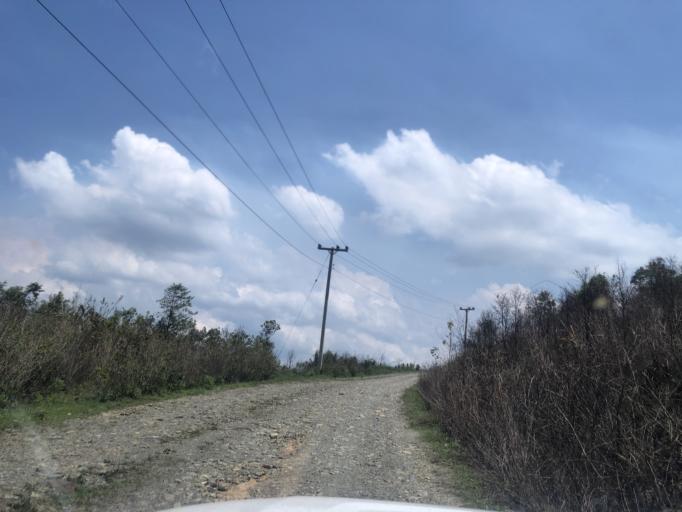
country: LA
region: Phongsali
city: Phongsali
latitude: 21.4205
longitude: 102.1845
